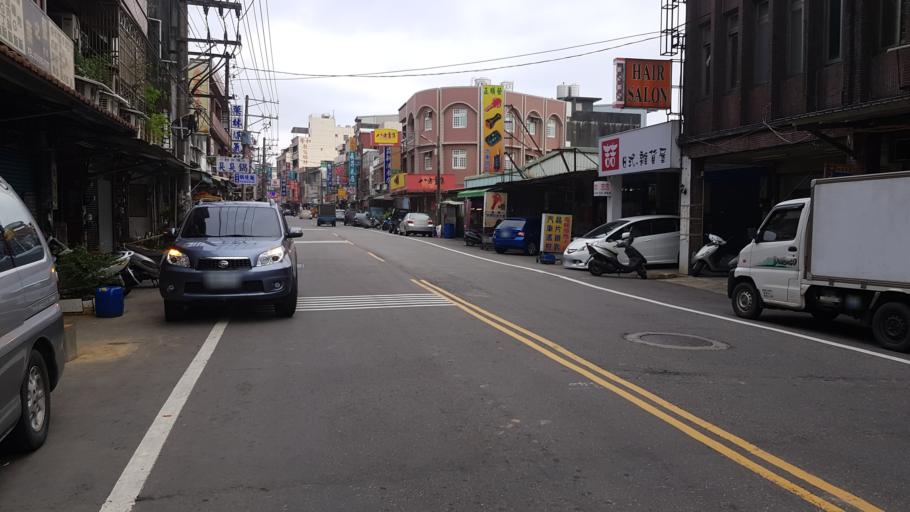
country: TW
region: Taiwan
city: Taoyuan City
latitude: 25.0780
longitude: 121.2577
